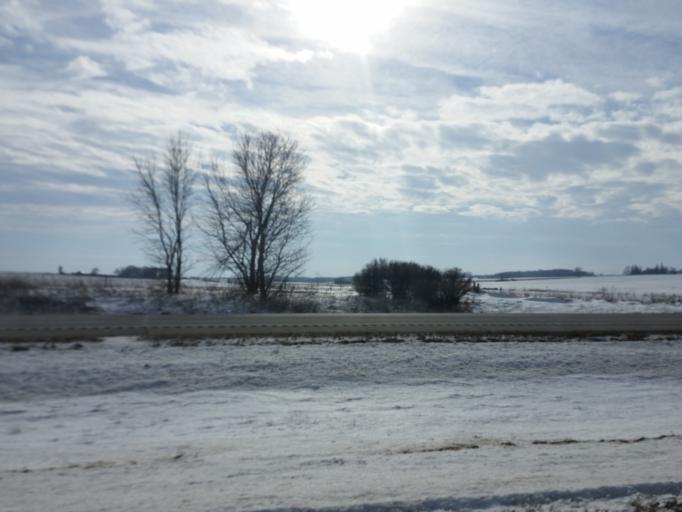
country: US
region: Iowa
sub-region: Buchanan County
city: Independence
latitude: 42.4619
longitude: -91.7628
